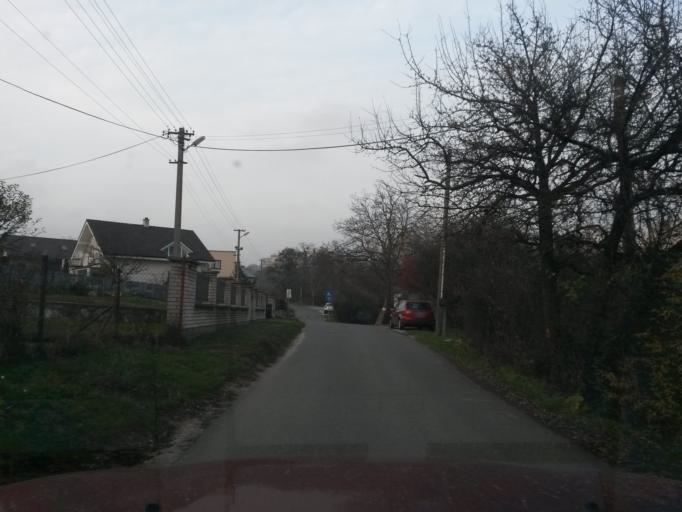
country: SK
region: Kosicky
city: Kosice
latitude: 48.7134
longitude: 21.2046
